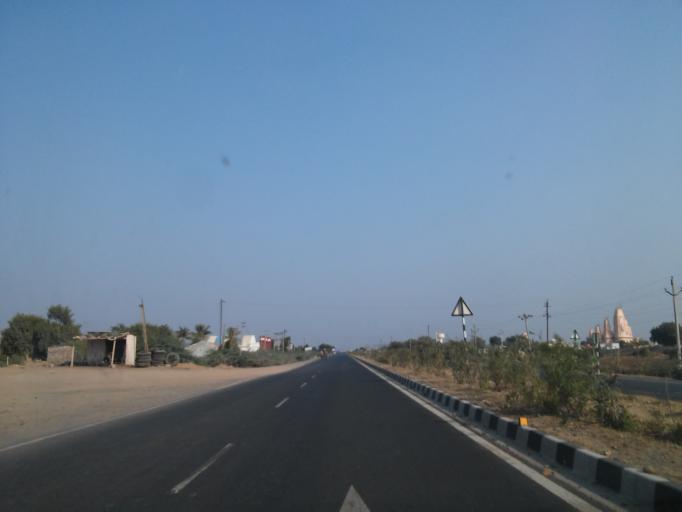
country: IN
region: Gujarat
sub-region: Surendranagar
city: Halvad
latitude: 23.0115
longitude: 71.2301
